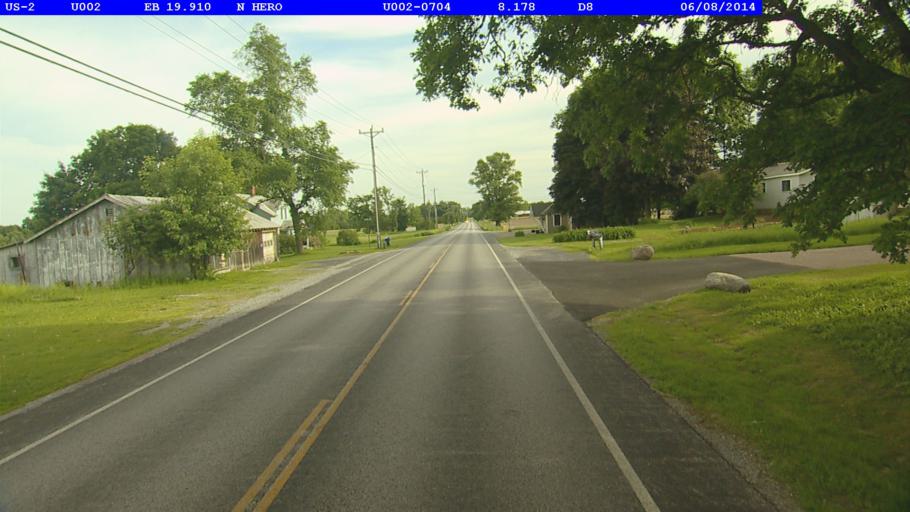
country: US
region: Vermont
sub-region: Grand Isle County
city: North Hero
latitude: 44.7820
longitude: -73.2935
